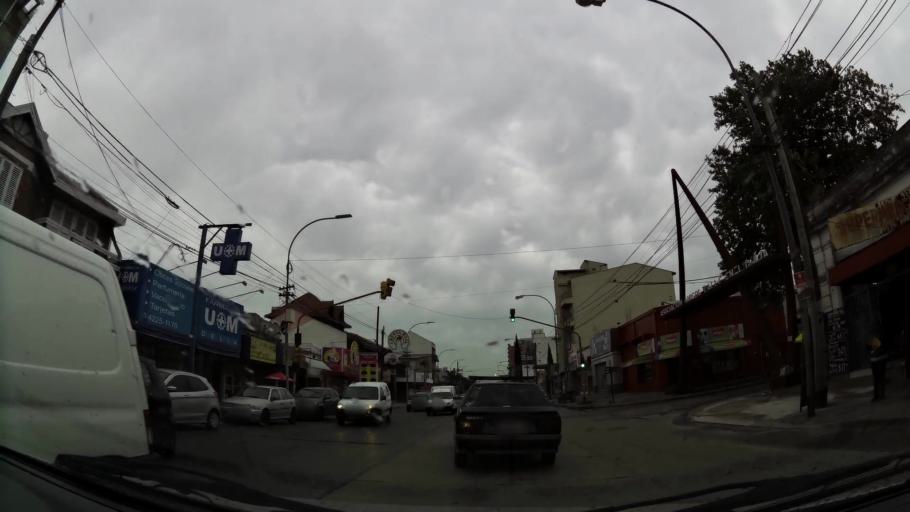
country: AR
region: Buenos Aires
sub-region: Partido de Lanus
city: Lanus
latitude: -34.6928
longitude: -58.4050
